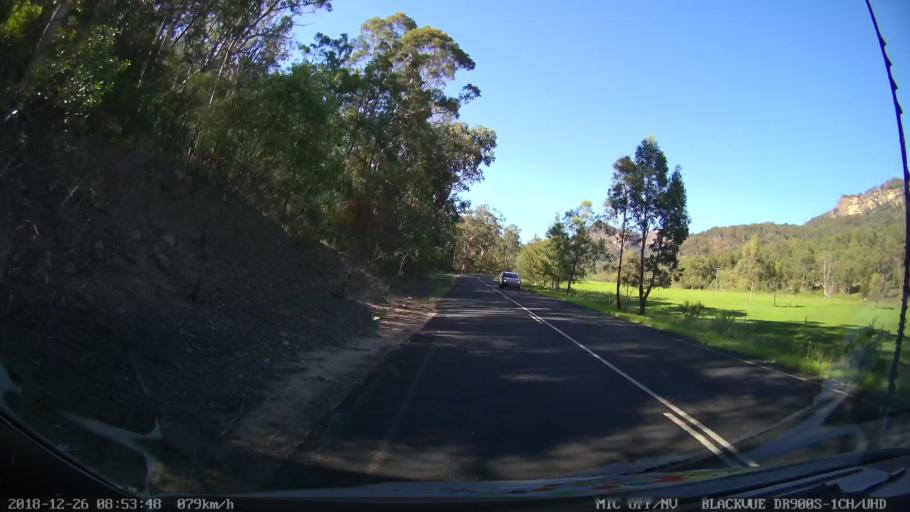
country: AU
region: New South Wales
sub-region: Mid-Western Regional
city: Kandos
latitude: -32.6083
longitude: 150.0758
